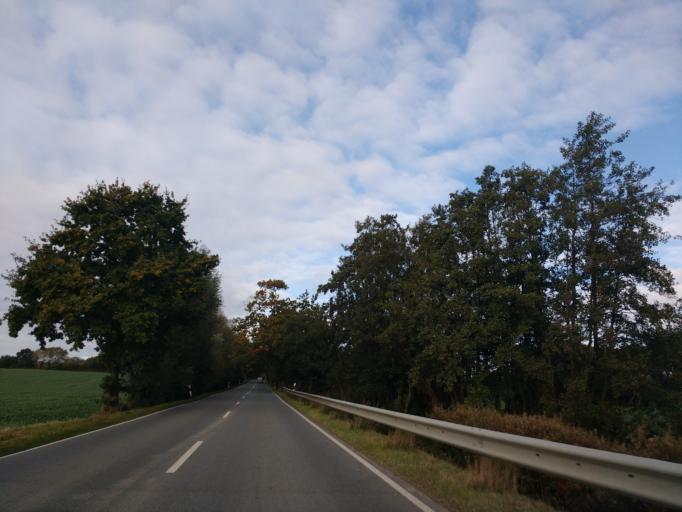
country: DE
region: Schleswig-Holstein
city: Altenkrempe
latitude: 54.1652
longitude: 10.7961
